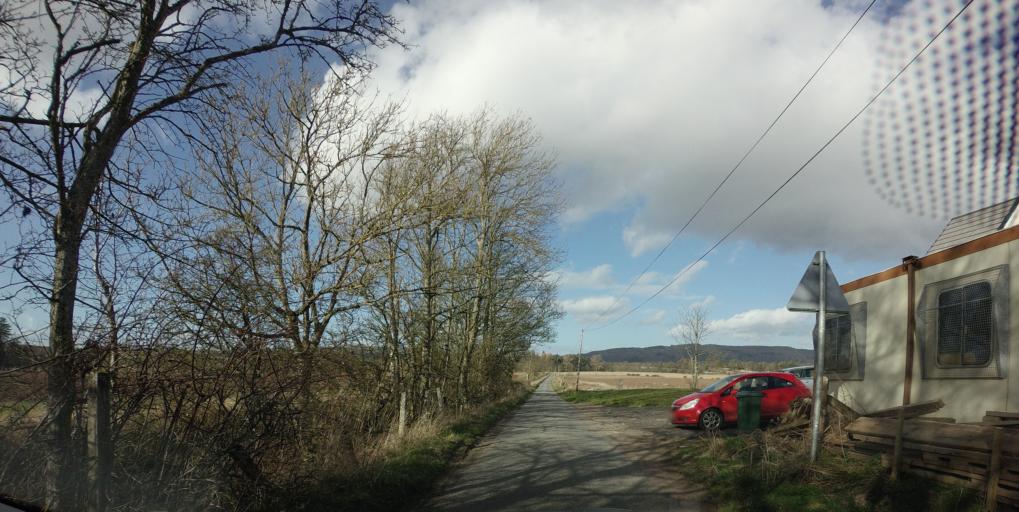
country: GB
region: Scotland
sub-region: Perth and Kinross
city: Bridge of Earn
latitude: 56.3314
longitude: -3.4297
